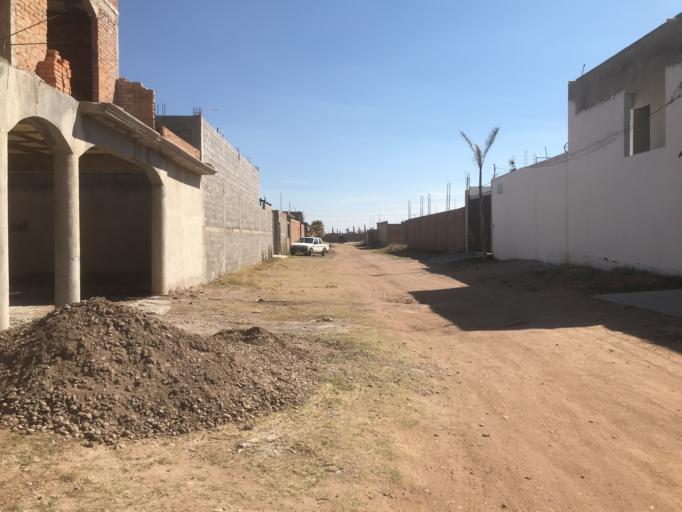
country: MX
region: Durango
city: Victoria de Durango
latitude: 24.0242
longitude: -104.5895
